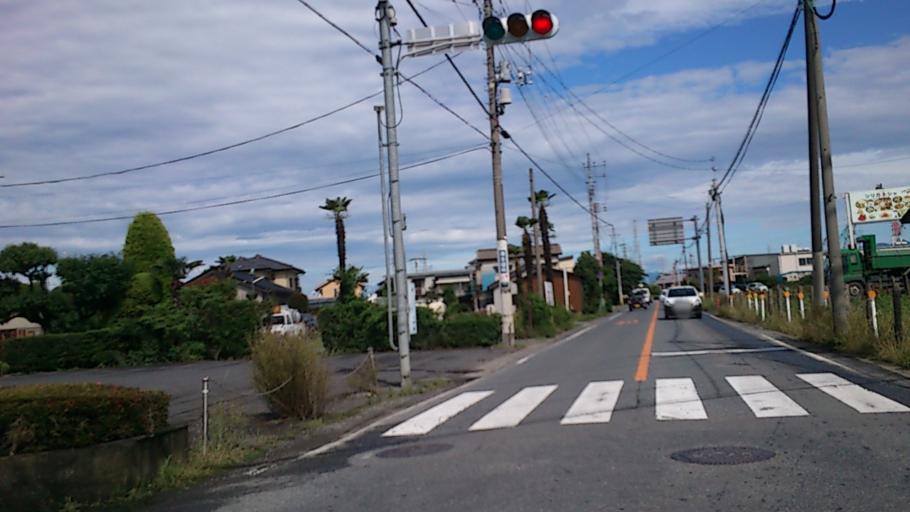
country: JP
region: Gunma
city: Fujioka
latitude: 36.2629
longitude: 139.0765
